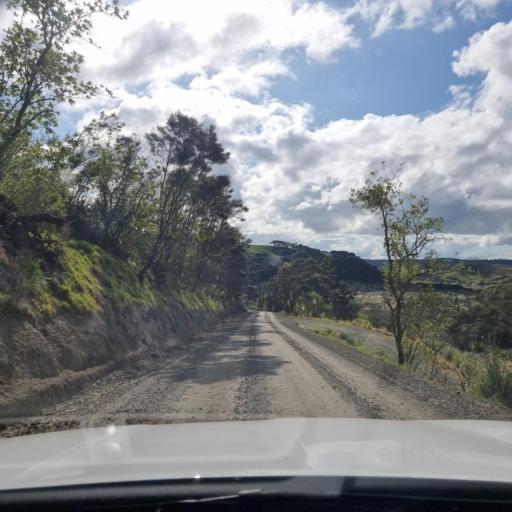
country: NZ
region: Auckland
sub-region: Auckland
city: Wellsford
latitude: -36.3081
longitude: 174.1228
